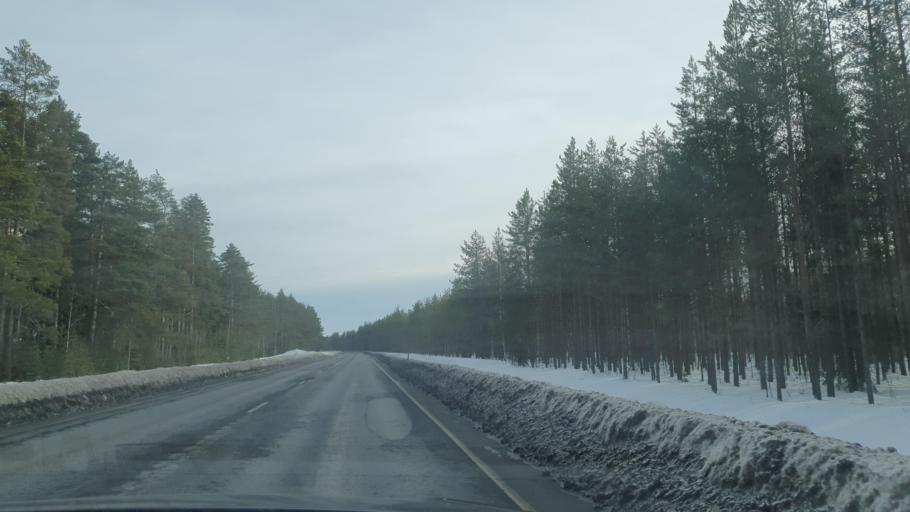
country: FI
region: Northern Ostrobothnia
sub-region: Oulunkaari
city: Utajaervi
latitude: 64.7304
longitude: 26.4823
